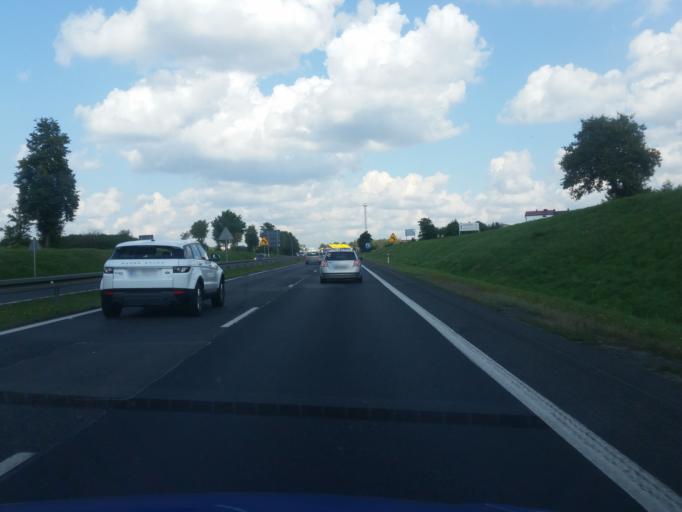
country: PL
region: Silesian Voivodeship
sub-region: Powiat myszkowski
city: Kozieglowy
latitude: 50.6017
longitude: 19.1515
